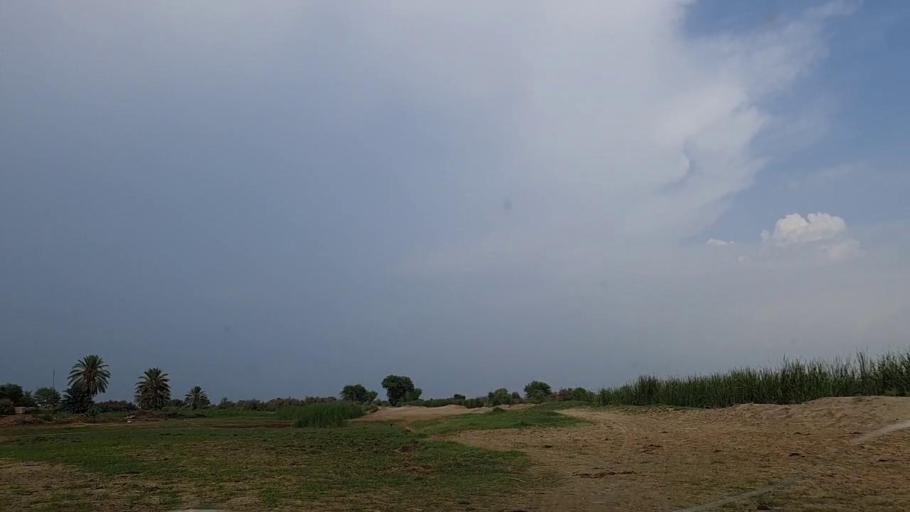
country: PK
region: Sindh
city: Khanpur
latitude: 27.8191
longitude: 69.5382
